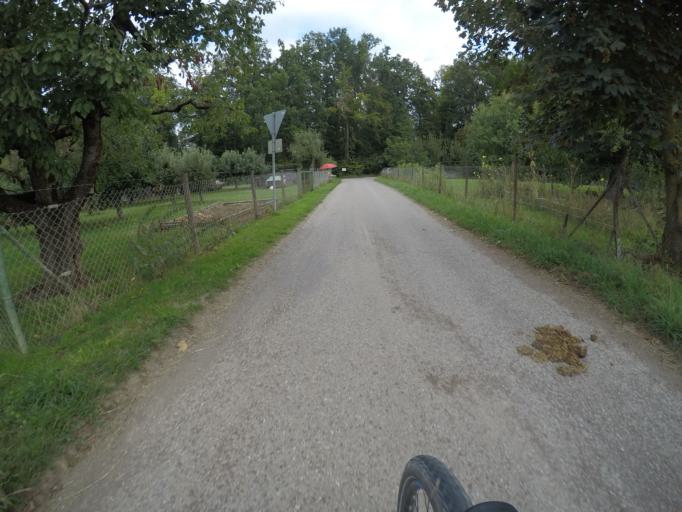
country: DE
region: Baden-Wuerttemberg
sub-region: Regierungsbezirk Stuttgart
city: Magstadt
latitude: 48.7334
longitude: 8.9370
